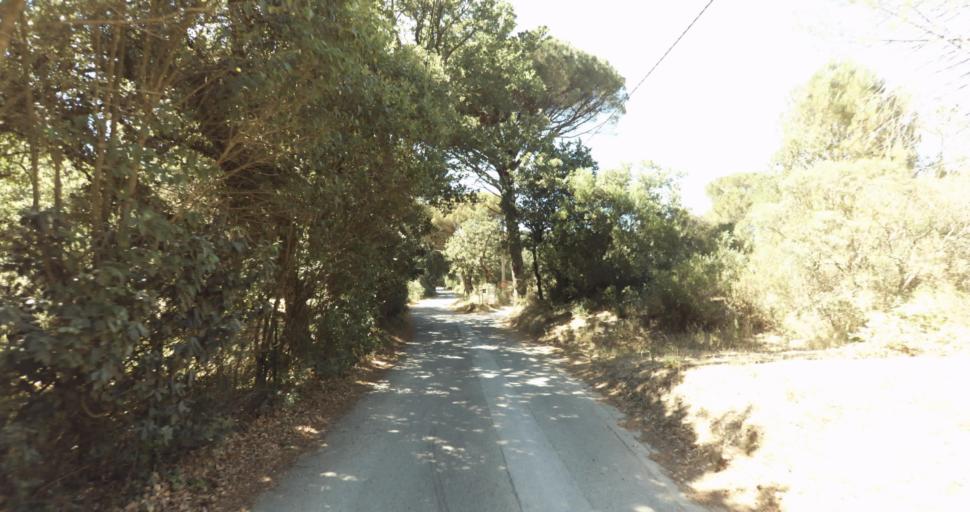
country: FR
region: Provence-Alpes-Cote d'Azur
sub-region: Departement du Var
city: Gassin
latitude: 43.2299
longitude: 6.5693
